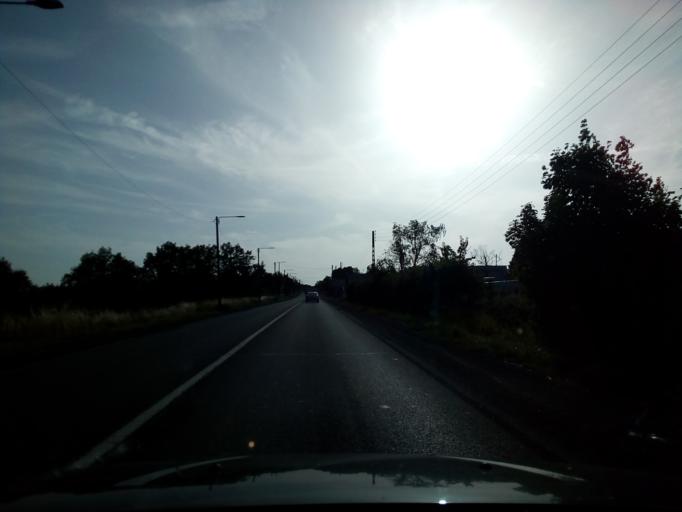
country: FR
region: Auvergne
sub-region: Departement de l'Allier
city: Premilhat
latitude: 46.3378
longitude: 2.5596
